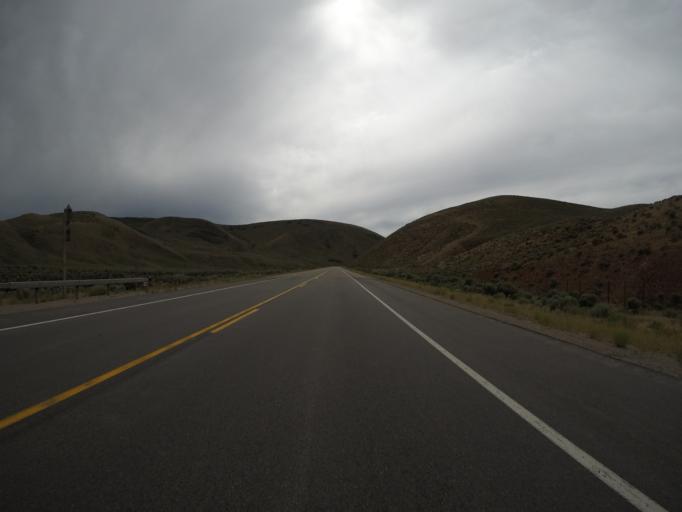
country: US
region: Wyoming
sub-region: Lincoln County
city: Kemmerer
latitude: 41.8241
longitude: -110.8286
